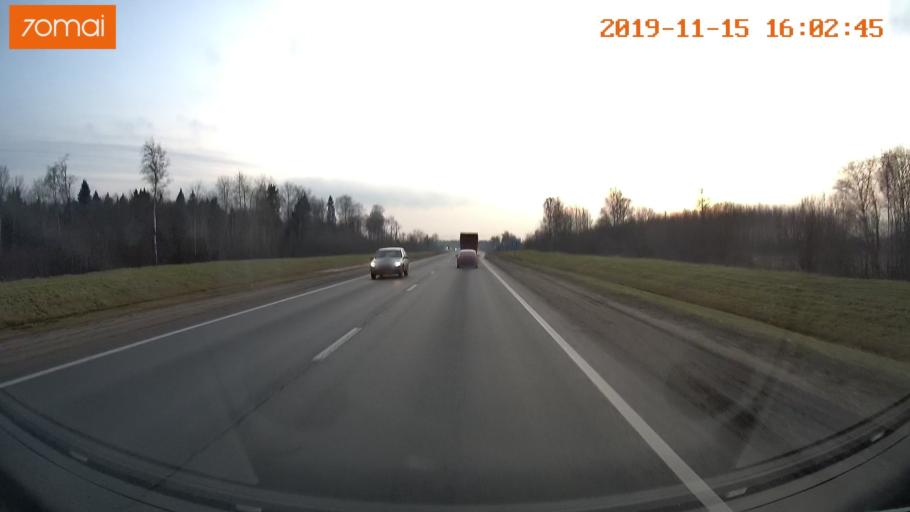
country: RU
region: Jaroslavl
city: Yaroslavl
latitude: 57.7680
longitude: 39.9216
